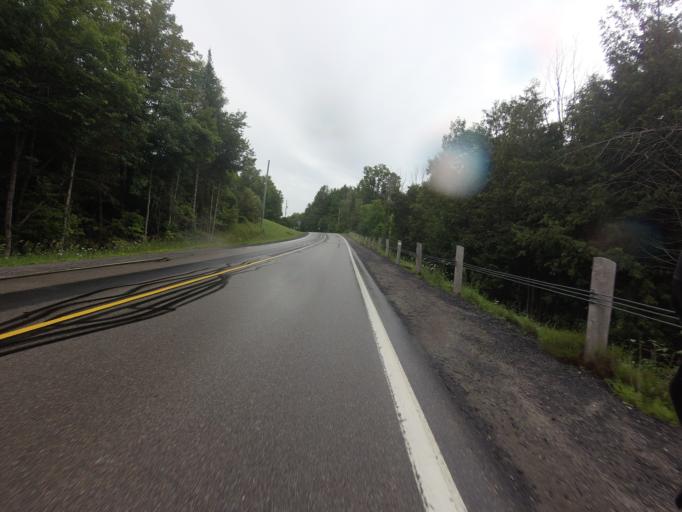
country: CA
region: Ontario
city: Perth
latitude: 44.9837
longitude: -76.3981
